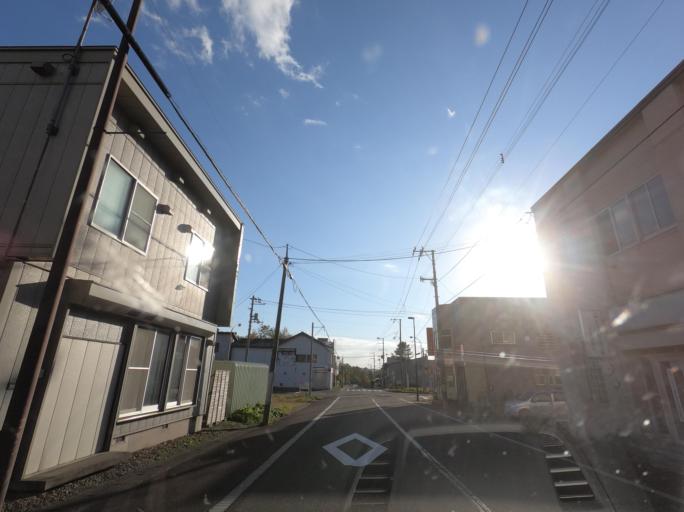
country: JP
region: Hokkaido
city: Iwamizawa
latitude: 43.0562
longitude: 141.9749
